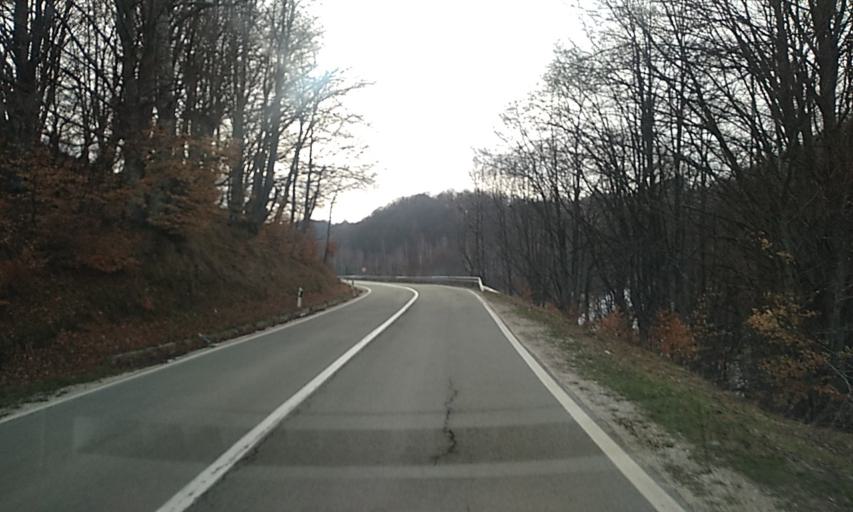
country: RS
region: Central Serbia
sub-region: Jablanicki Okrug
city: Crna Trava
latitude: 42.6793
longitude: 22.3611
